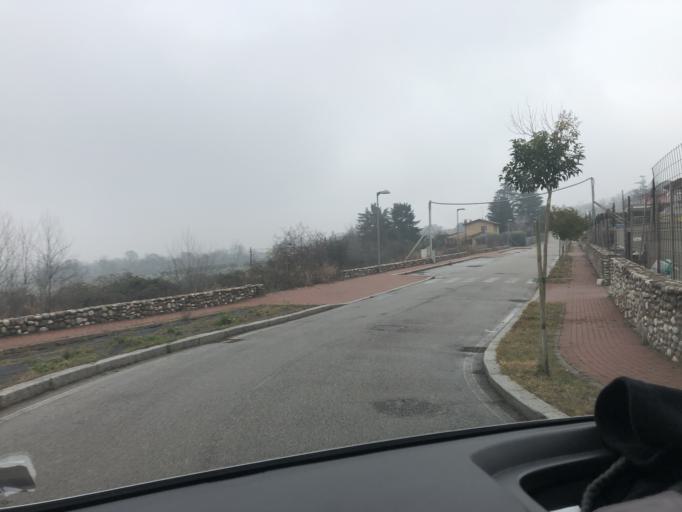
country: IT
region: Veneto
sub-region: Provincia di Verona
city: Sona
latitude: 45.4351
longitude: 10.8369
